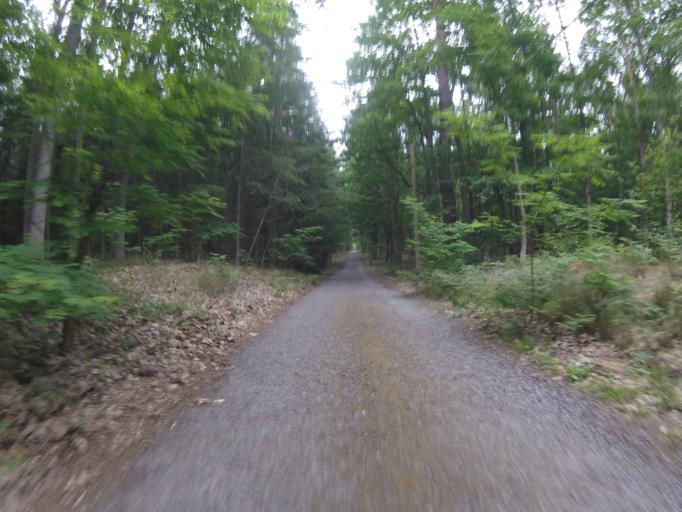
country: DE
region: Brandenburg
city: Gross Koris
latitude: 52.2148
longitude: 13.7039
